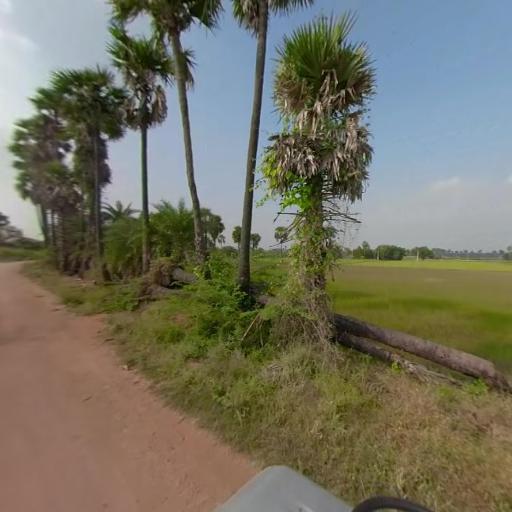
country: IN
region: Telangana
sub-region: Nalgonda
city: Suriapet
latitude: 17.2006
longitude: 79.4879
